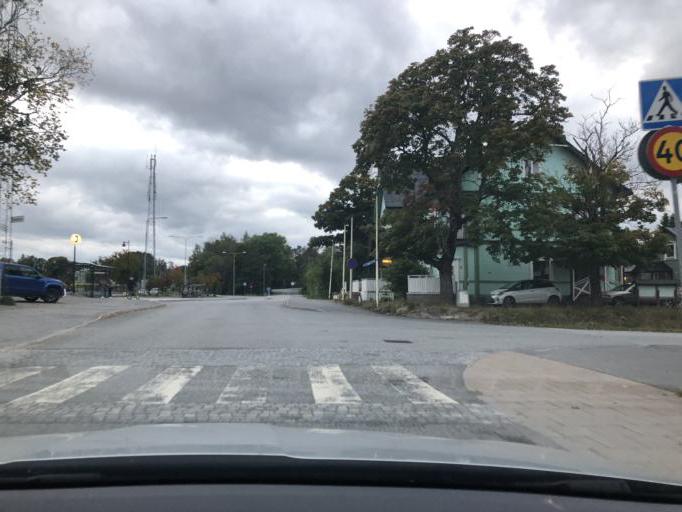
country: SE
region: Stockholm
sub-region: Haninge Kommun
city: Jordbro
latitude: 59.1030
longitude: 18.0450
